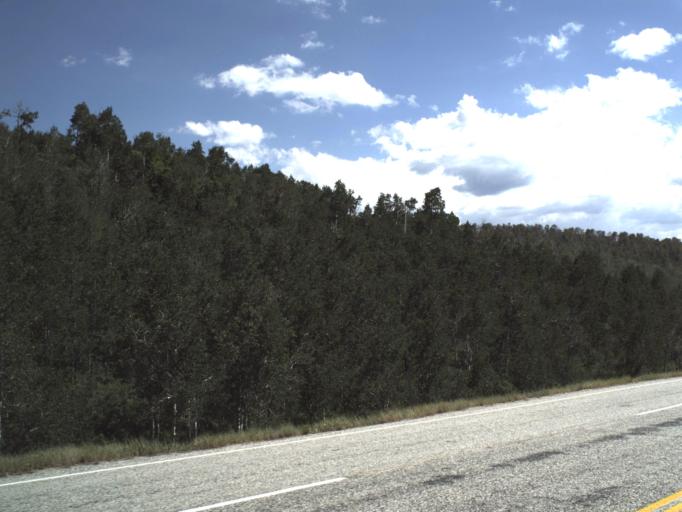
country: US
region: Utah
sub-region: Weber County
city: Wolf Creek
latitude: 41.4224
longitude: -111.5645
